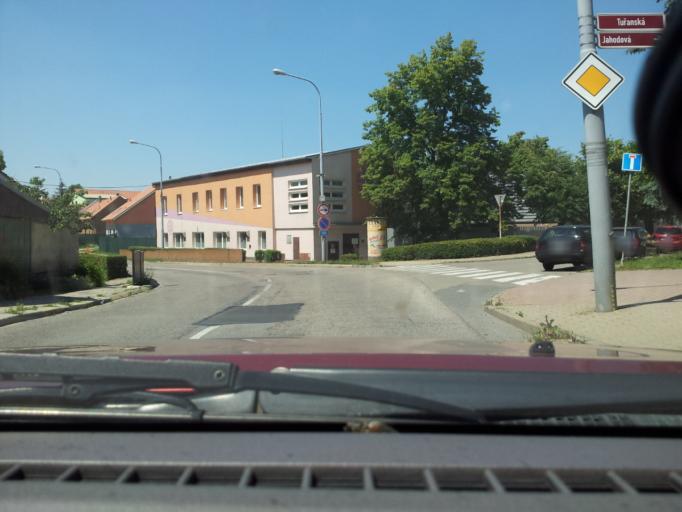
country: CZ
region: South Moravian
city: Modrice
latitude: 49.1521
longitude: 16.6558
